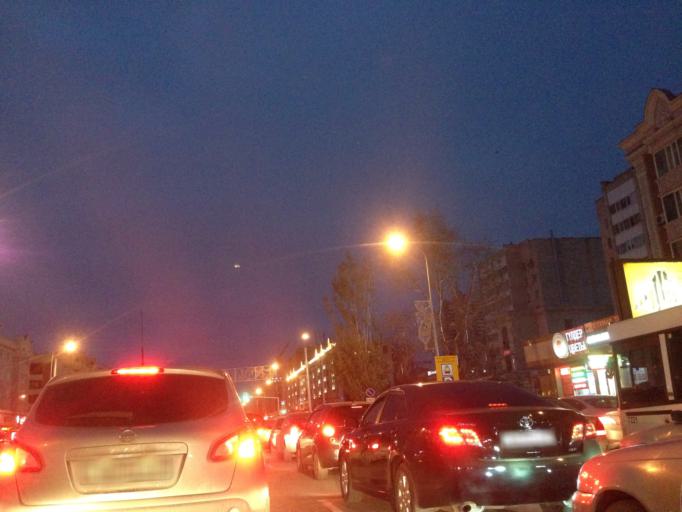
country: KZ
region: Astana Qalasy
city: Astana
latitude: 51.1597
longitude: 71.4290
